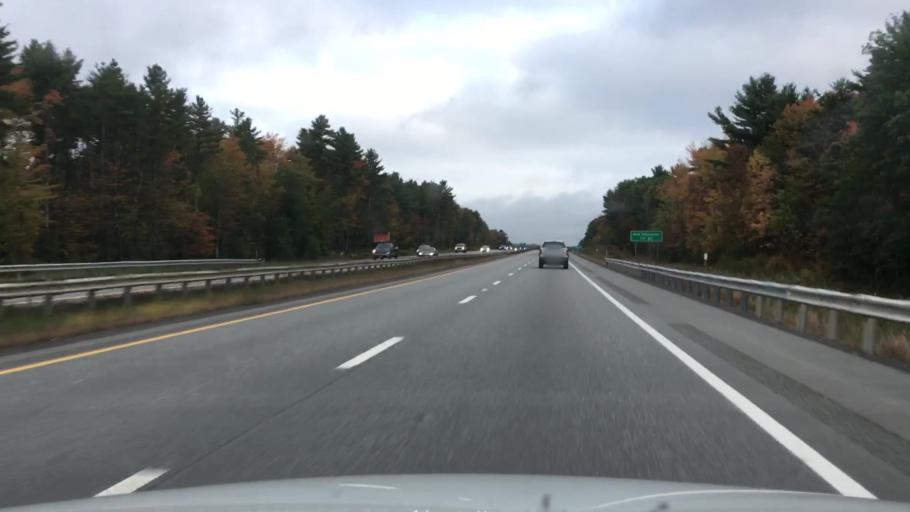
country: US
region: Maine
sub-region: Cumberland County
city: Cumberland Center
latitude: 43.8713
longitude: -70.3287
